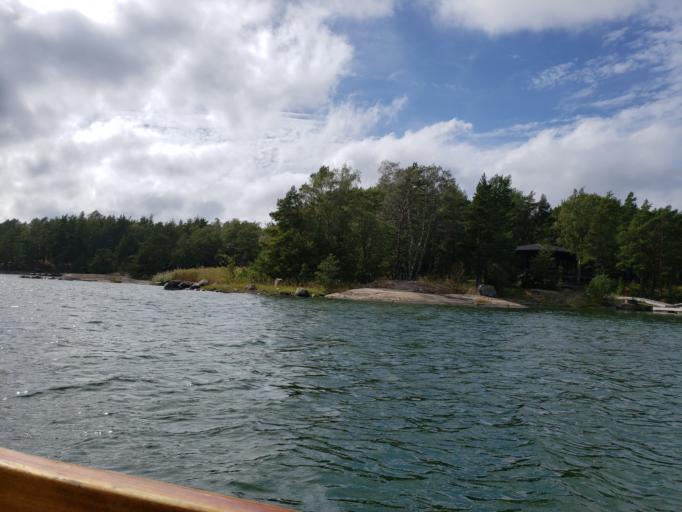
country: FI
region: Varsinais-Suomi
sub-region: Aboland-Turunmaa
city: Dragsfjaerd
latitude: 59.9112
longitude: 22.3770
